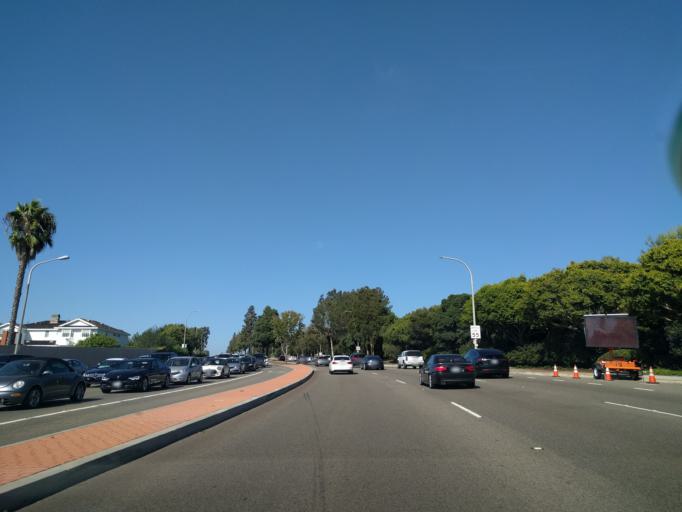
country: US
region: California
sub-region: Orange County
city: San Joaquin Hills
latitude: 33.6314
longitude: -117.8742
